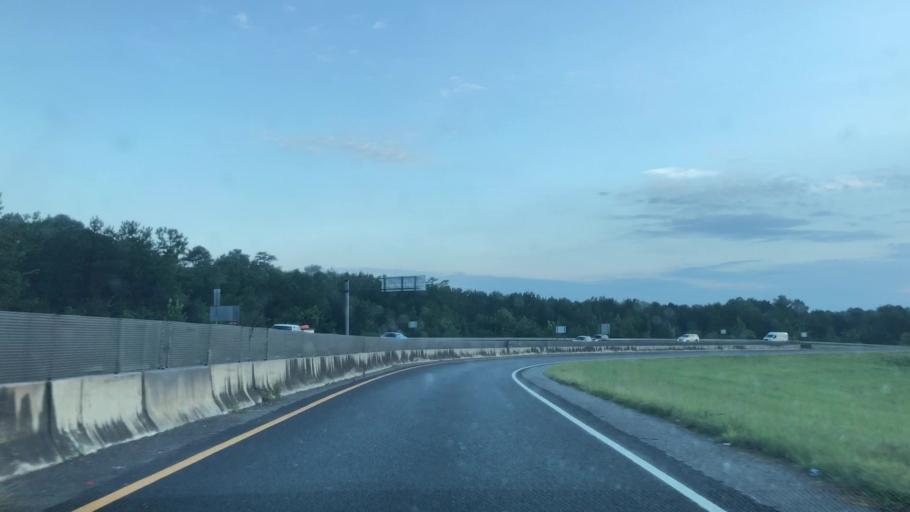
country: US
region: Alabama
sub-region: Shelby County
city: Indian Springs Village
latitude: 33.3541
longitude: -86.7812
